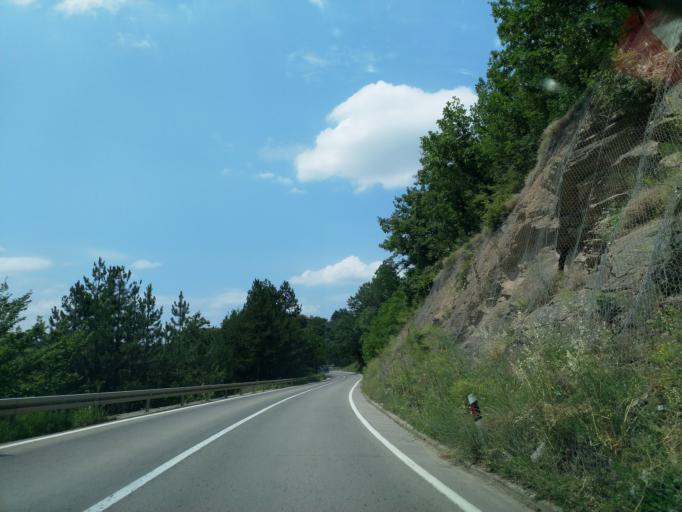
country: RS
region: Central Serbia
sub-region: Rasinski Okrug
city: Aleksandrovac
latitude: 43.4149
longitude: 21.1764
